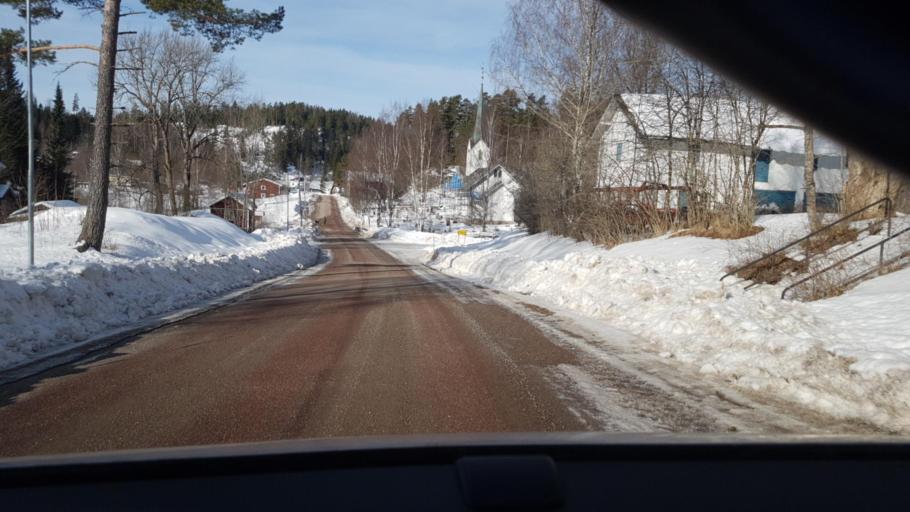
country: NO
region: Hedmark
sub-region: Eidskog
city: Skotterud
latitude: 59.8176
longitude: 12.0174
